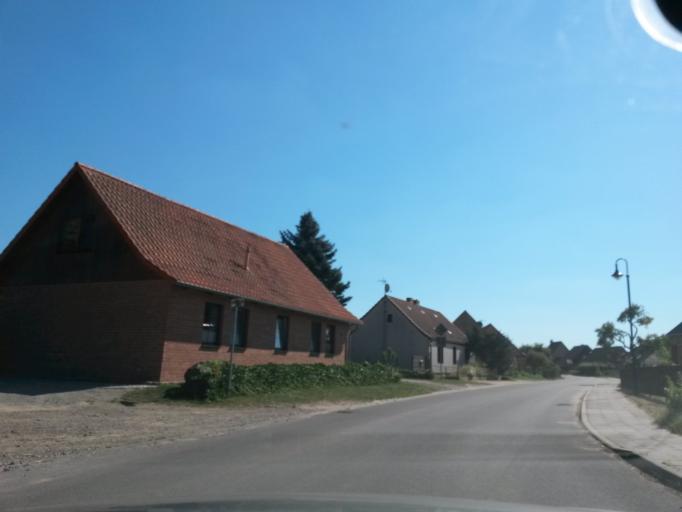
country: DE
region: Brandenburg
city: Templin
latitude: 53.1735
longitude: 13.4331
